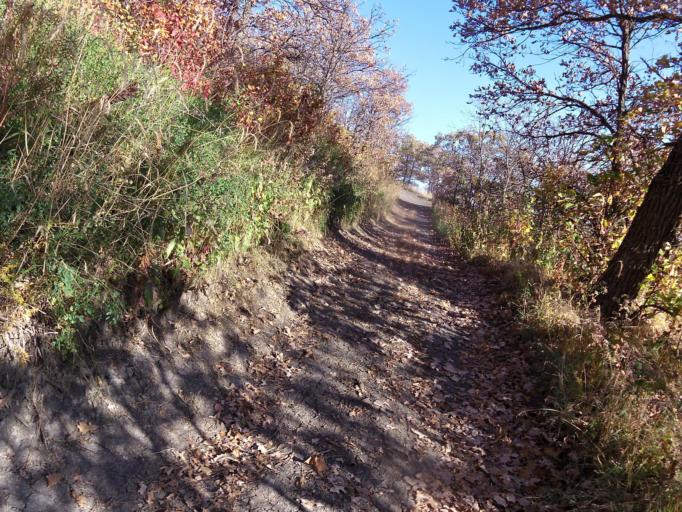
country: CA
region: Manitoba
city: Morden
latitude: 48.9407
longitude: -98.0673
